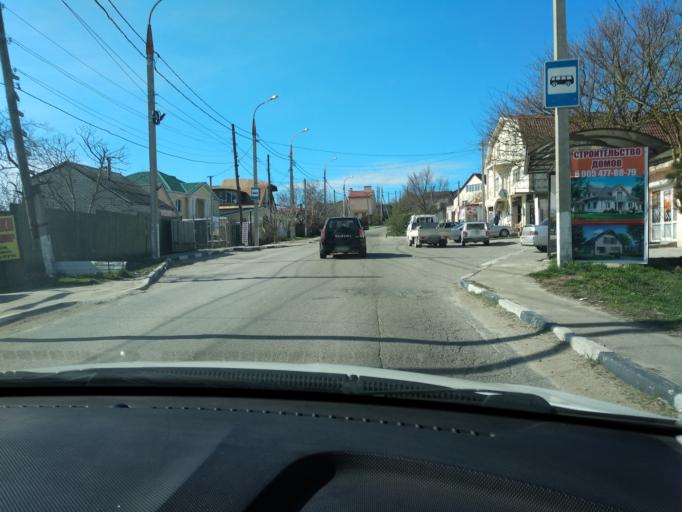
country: RU
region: Krasnodarskiy
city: Myskhako
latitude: 44.7037
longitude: 37.7420
